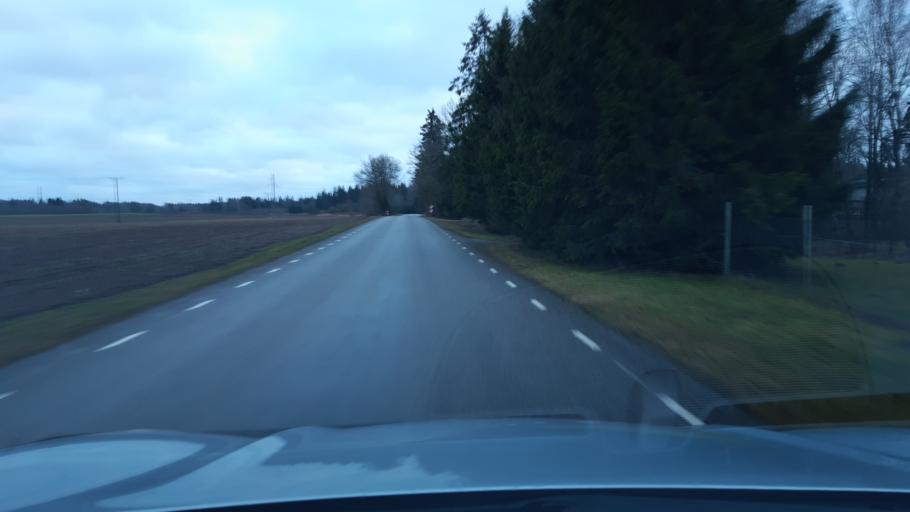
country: EE
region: Harju
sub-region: Saue linn
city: Saue
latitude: 59.2247
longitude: 24.5229
